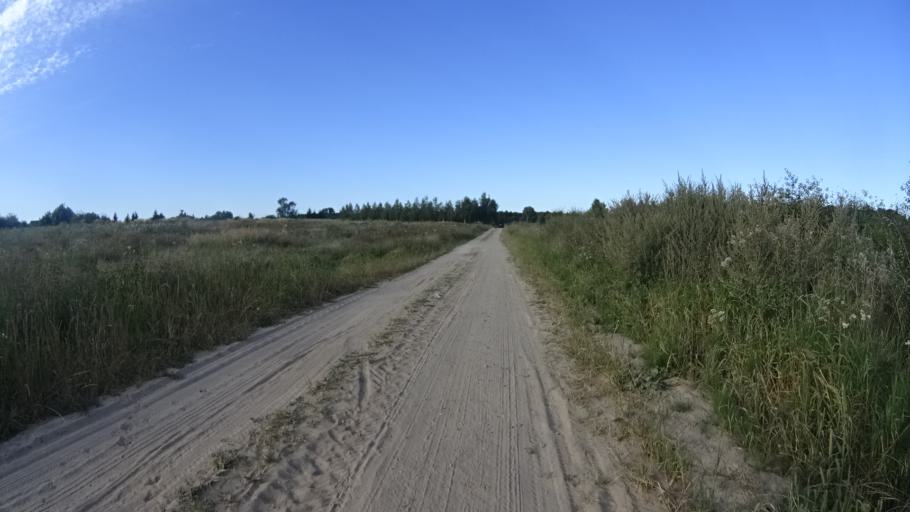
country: PL
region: Masovian Voivodeship
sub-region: Powiat grojecki
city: Goszczyn
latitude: 51.6909
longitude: 20.8151
